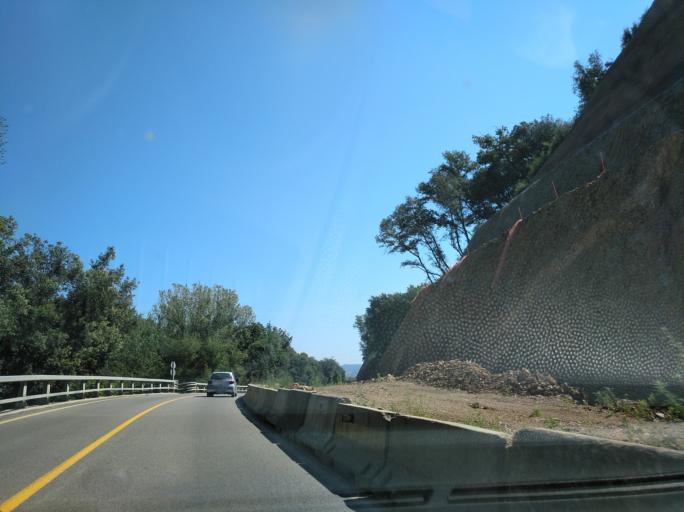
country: ES
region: Catalonia
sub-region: Provincia de Girona
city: Bescano
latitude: 41.9697
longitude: 2.7511
